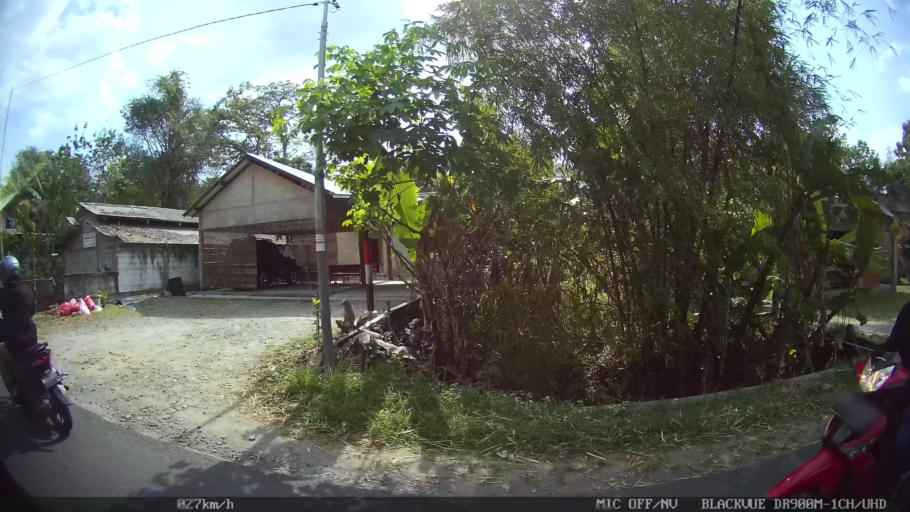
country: ID
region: Daerah Istimewa Yogyakarta
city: Kasihan
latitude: -7.8507
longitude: 110.3141
